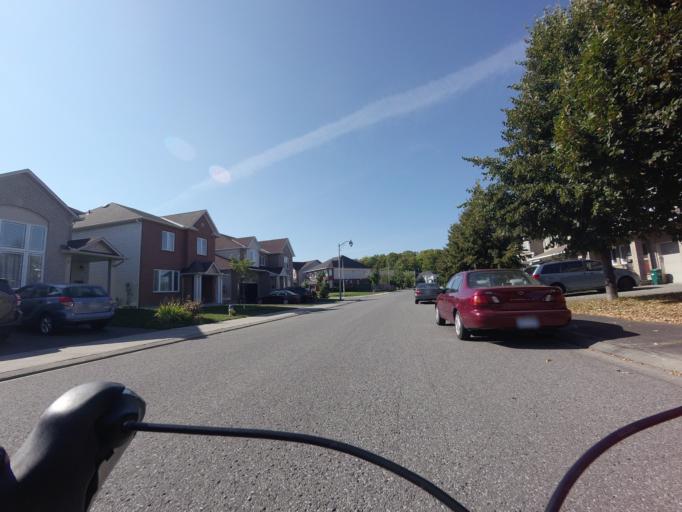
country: CA
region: Ontario
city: Bells Corners
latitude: 45.2702
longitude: -75.7101
